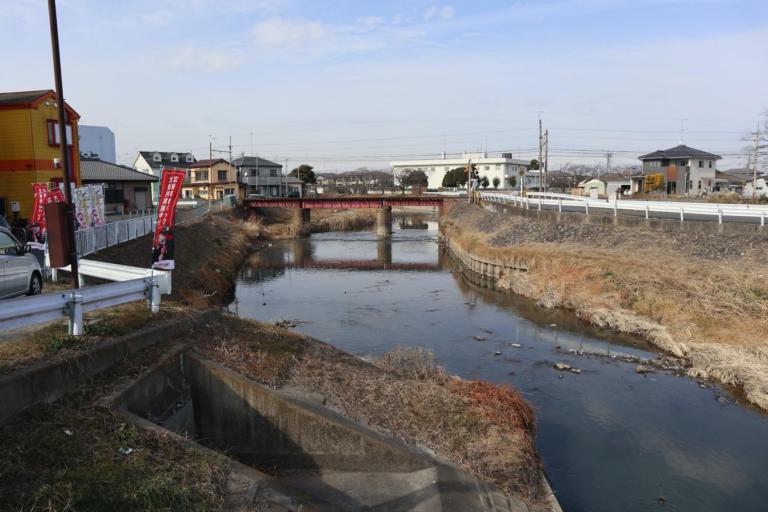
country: JP
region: Saitama
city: Gyoda
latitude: 36.1435
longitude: 139.4643
